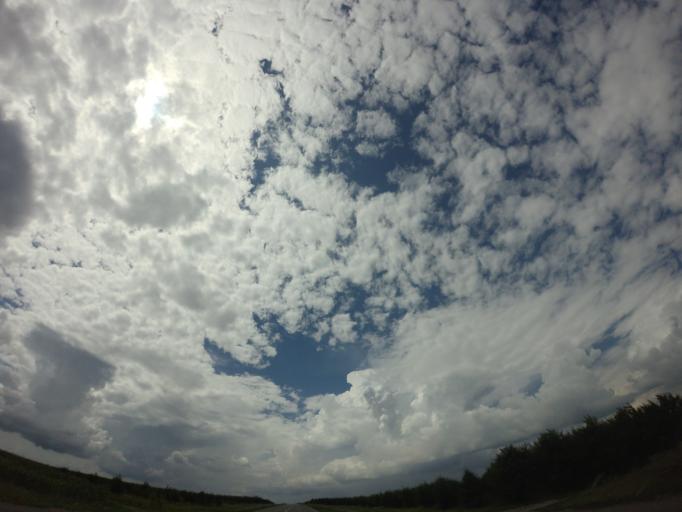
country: PL
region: Lublin Voivodeship
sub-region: Powiat opolski
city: Laziska
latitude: 51.1287
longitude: 21.8415
